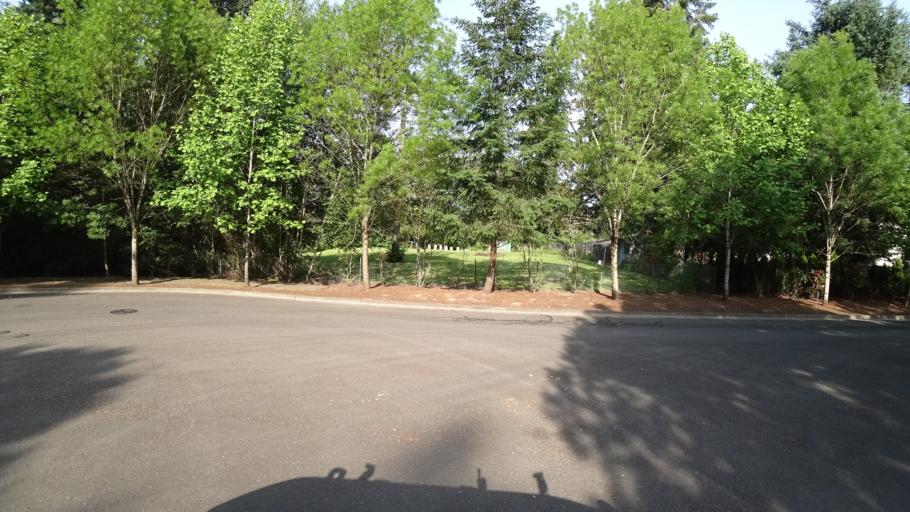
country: US
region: Oregon
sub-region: Clackamas County
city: Happy Valley
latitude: 45.4443
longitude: -122.5275
